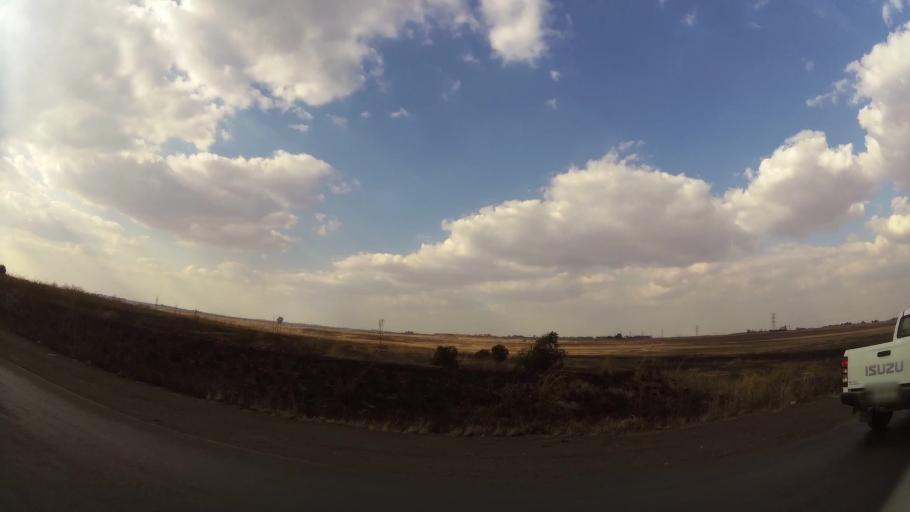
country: ZA
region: Mpumalanga
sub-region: Nkangala District Municipality
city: Delmas
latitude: -26.1744
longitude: 28.6987
